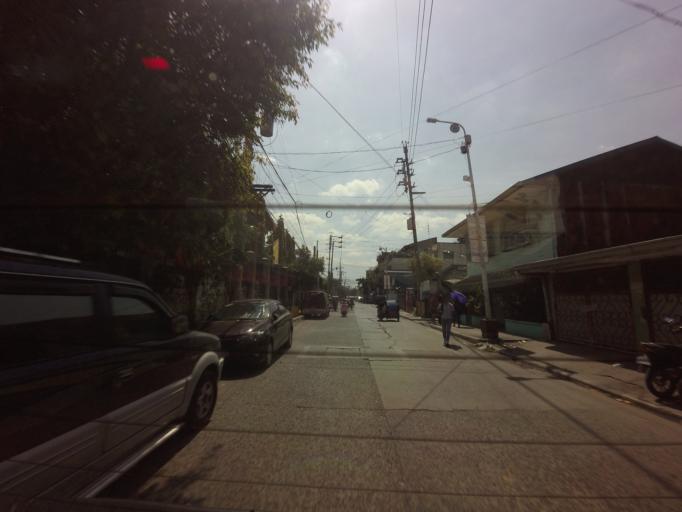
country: PH
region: Metro Manila
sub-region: City of Manila
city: Manila
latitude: 14.6241
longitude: 120.9644
